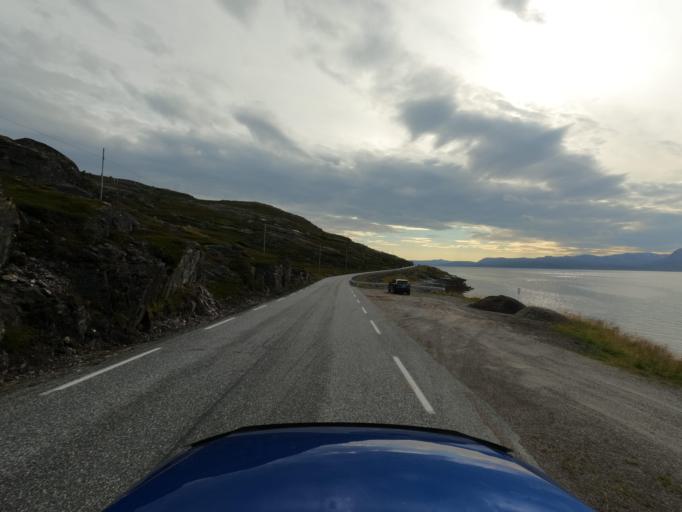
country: NO
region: Finnmark Fylke
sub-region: Hammerfest
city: Rypefjord
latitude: 70.5942
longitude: 23.6812
